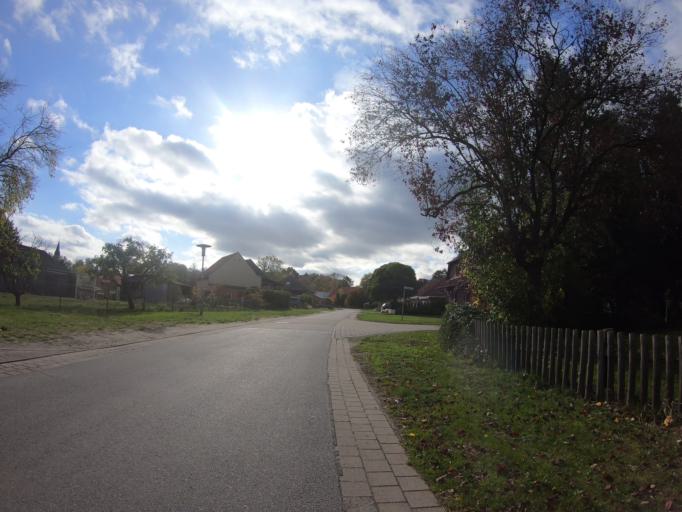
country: DE
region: Lower Saxony
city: Ribbesbuttel
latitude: 52.4336
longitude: 10.5065
